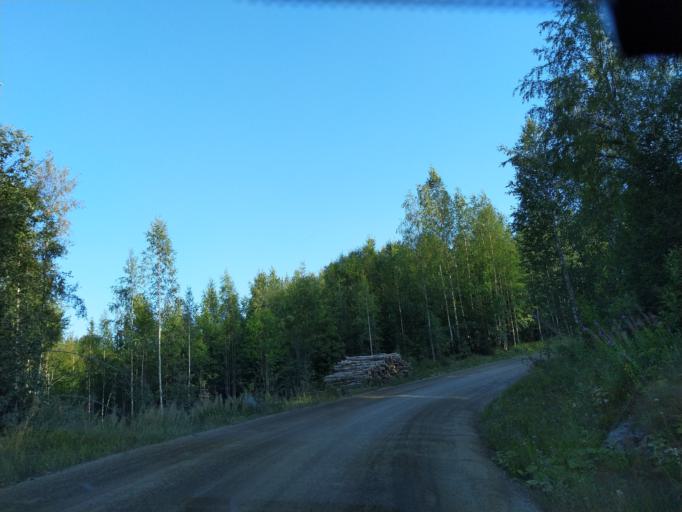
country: FI
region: Central Finland
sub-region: Jaemsae
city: Kuhmoinen
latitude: 61.6342
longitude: 25.0934
